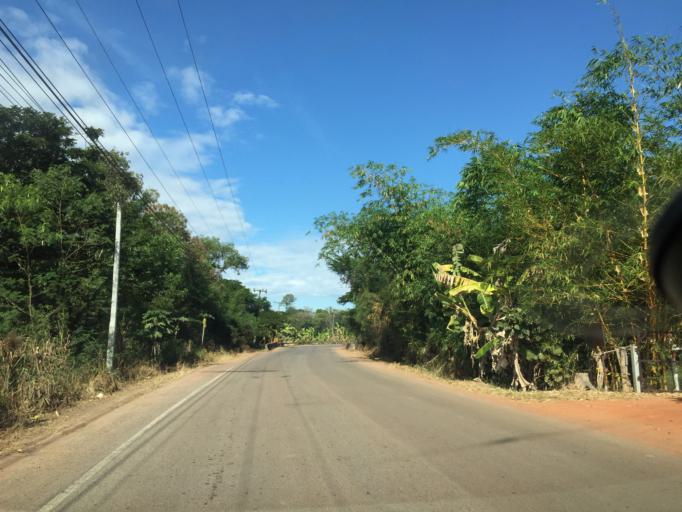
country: TH
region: Kalasin
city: Tha Khantho
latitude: 16.9737
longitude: 103.2627
